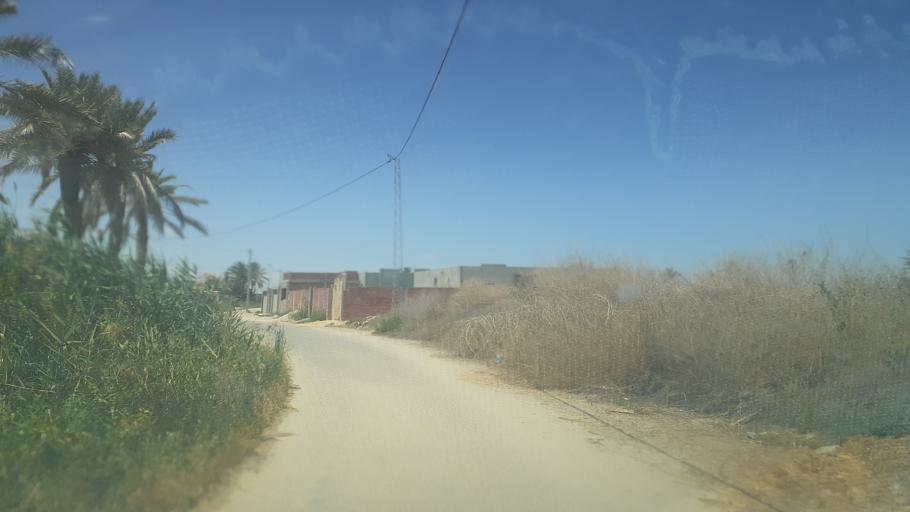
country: TN
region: Qabis
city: Gabes
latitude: 33.9293
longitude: 10.0600
